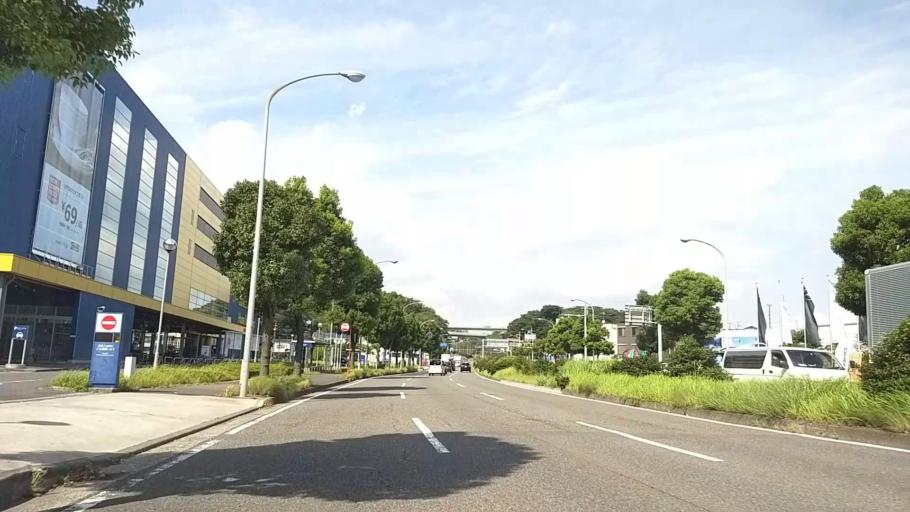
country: JP
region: Kanagawa
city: Yokohama
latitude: 35.5220
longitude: 139.5909
